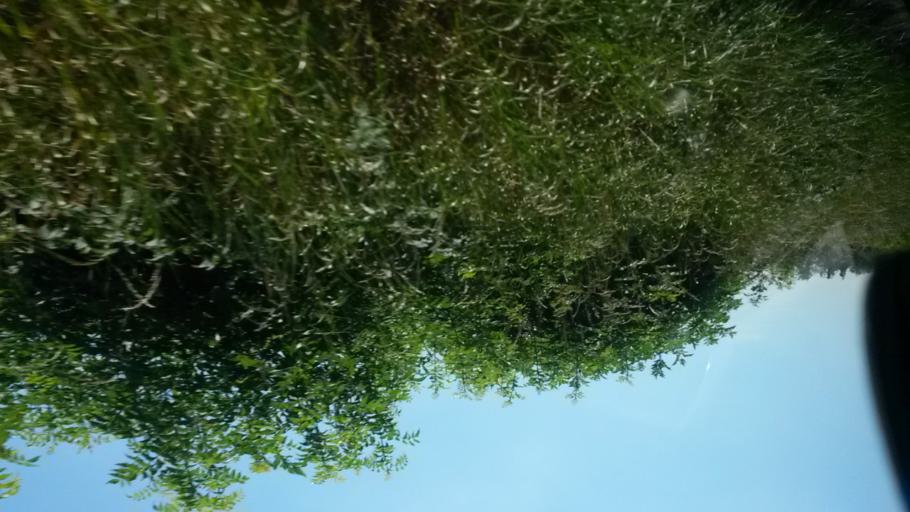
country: IE
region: Leinster
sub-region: An Mhi
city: Stamullin
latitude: 53.5679
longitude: -6.3157
